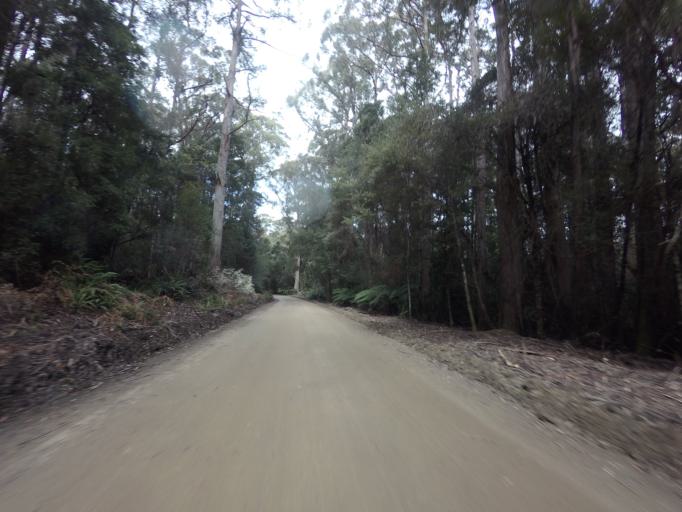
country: AU
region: Tasmania
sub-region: Huon Valley
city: Geeveston
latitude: -43.4003
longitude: 146.8614
